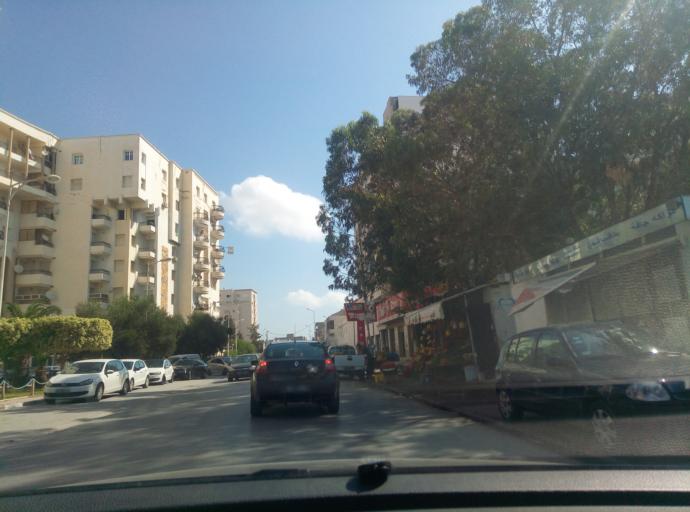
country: TN
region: Tunis
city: La Goulette
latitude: 36.8600
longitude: 10.2726
